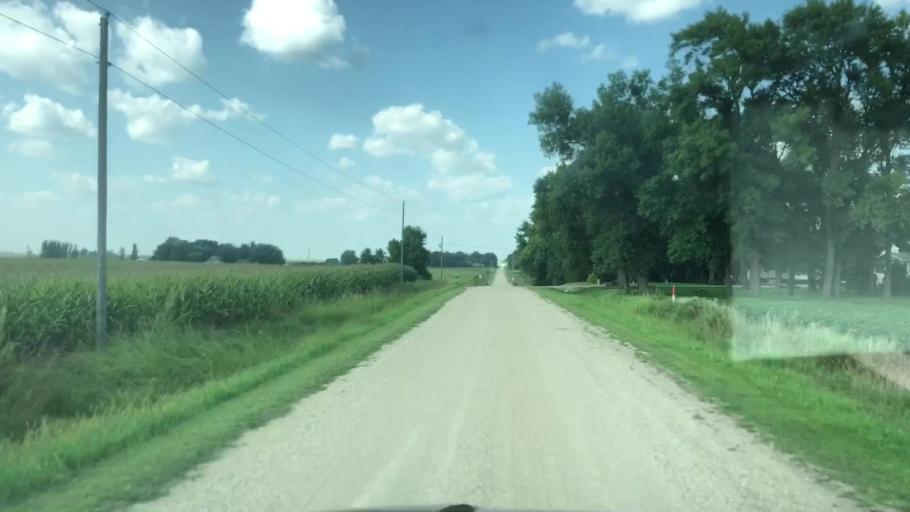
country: US
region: Iowa
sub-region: O'Brien County
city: Sheldon
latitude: 43.1657
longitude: -95.7822
